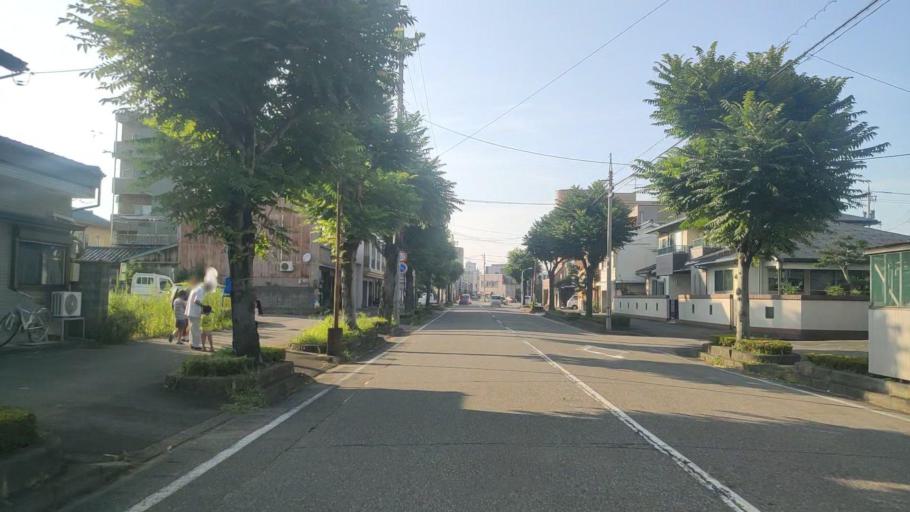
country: JP
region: Fukui
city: Fukui-shi
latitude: 36.0547
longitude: 136.2305
